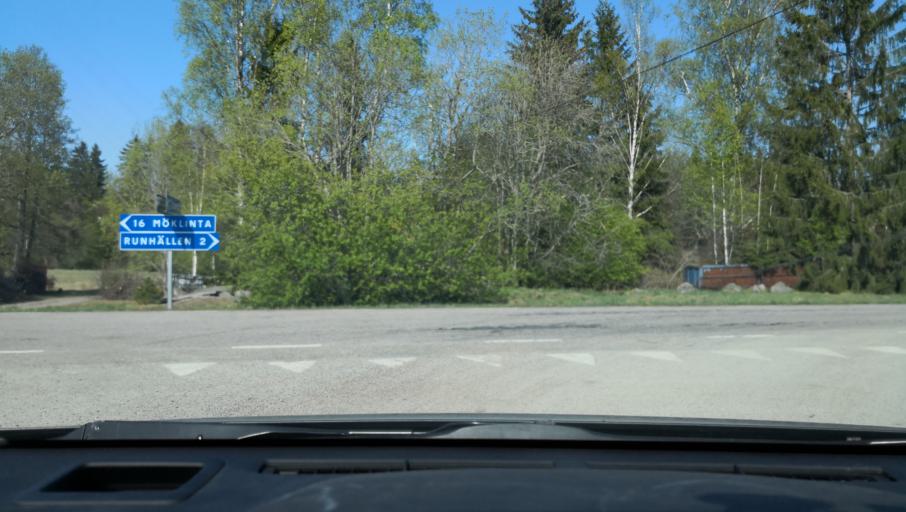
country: SE
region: Uppsala
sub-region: Heby Kommun
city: Heby
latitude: 60.0358
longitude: 16.7838
